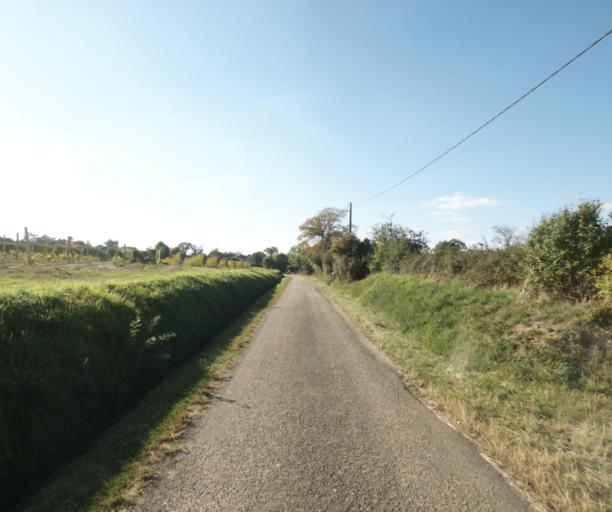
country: FR
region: Midi-Pyrenees
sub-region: Departement du Gers
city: Eauze
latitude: 43.7971
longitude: 0.1413
